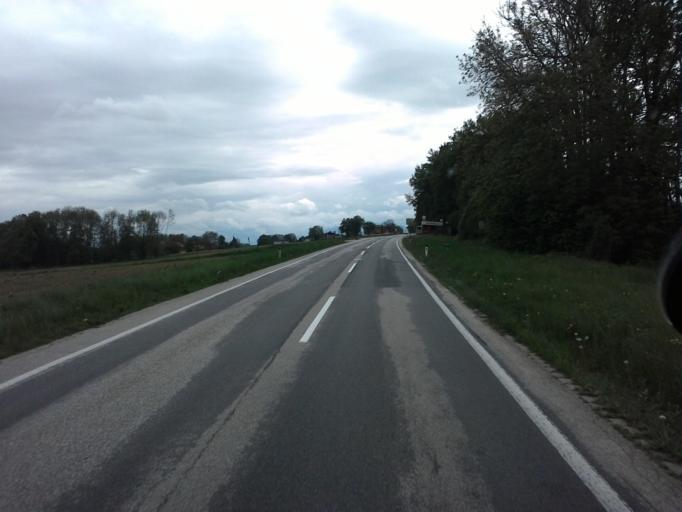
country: AT
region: Upper Austria
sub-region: Wels-Land
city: Sattledt
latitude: 48.0216
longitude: 14.0603
